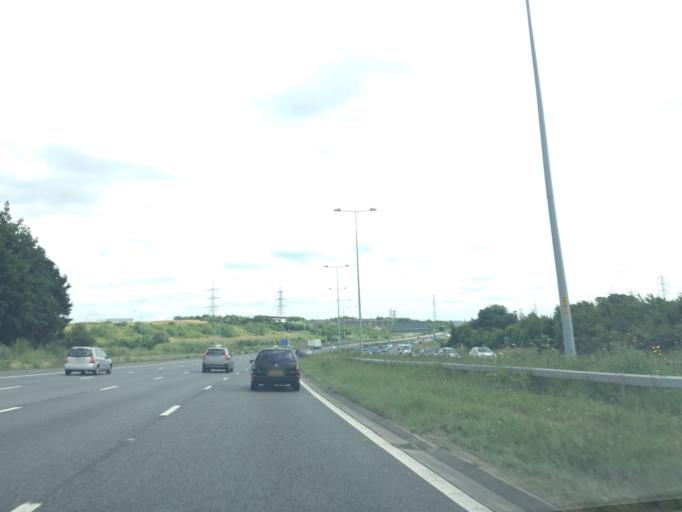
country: GB
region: England
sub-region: Kent
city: Swanscombe
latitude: 51.4303
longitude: 0.3207
